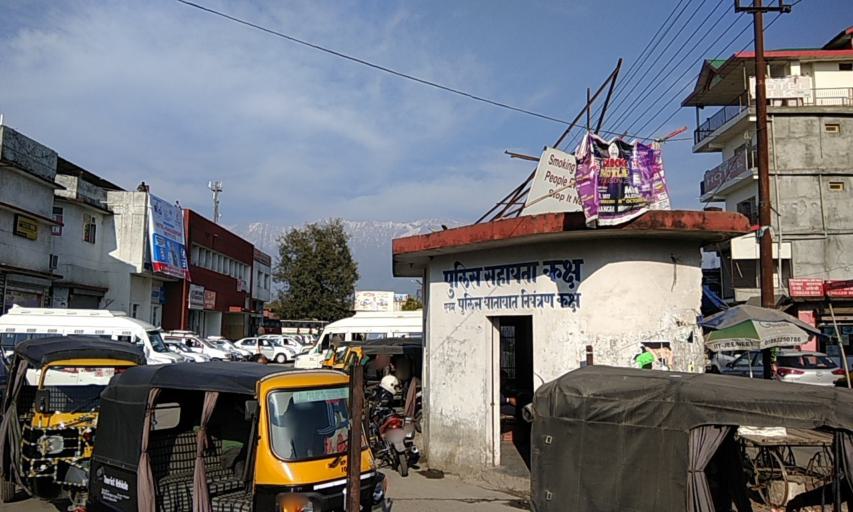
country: IN
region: Himachal Pradesh
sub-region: Kangra
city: Kangra
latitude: 32.1102
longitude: 76.2780
